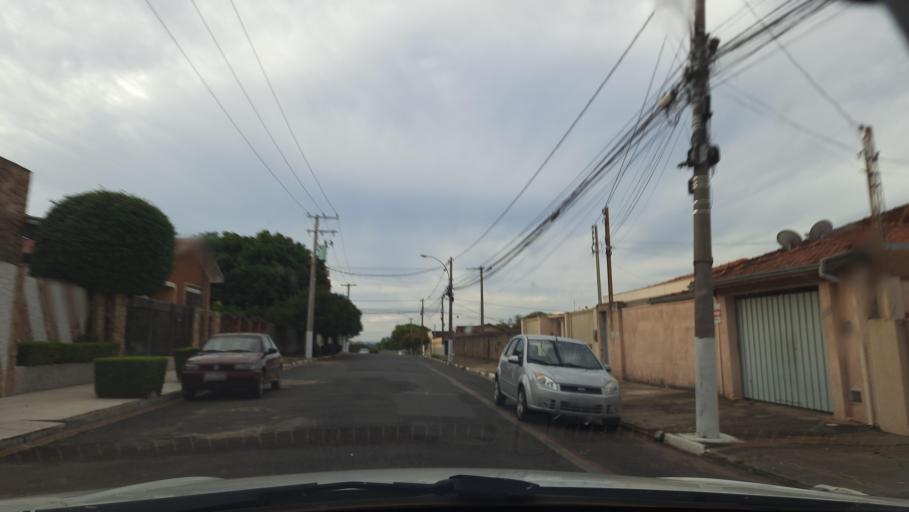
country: BR
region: Sao Paulo
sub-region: Casa Branca
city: Casa Branca
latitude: -21.7771
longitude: -47.0747
